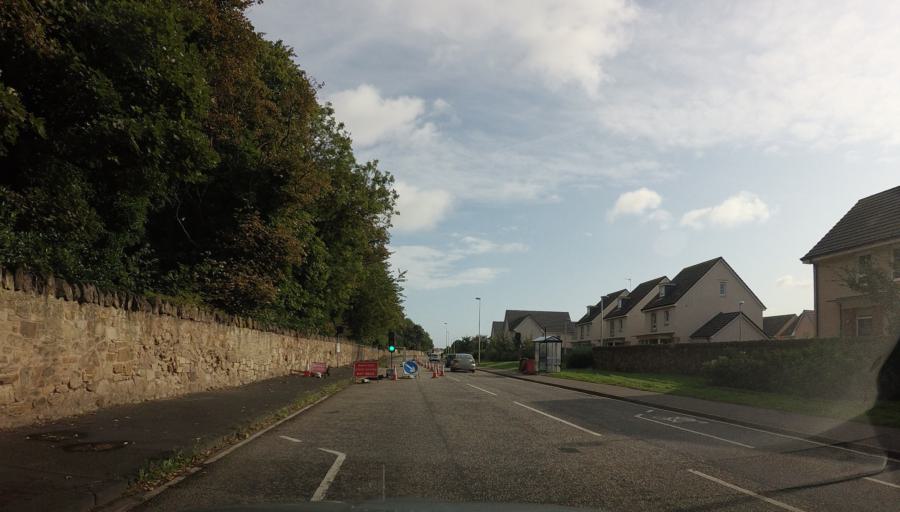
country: GB
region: Scotland
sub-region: East Lothian
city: Prestonpans
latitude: 55.9503
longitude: -2.9939
